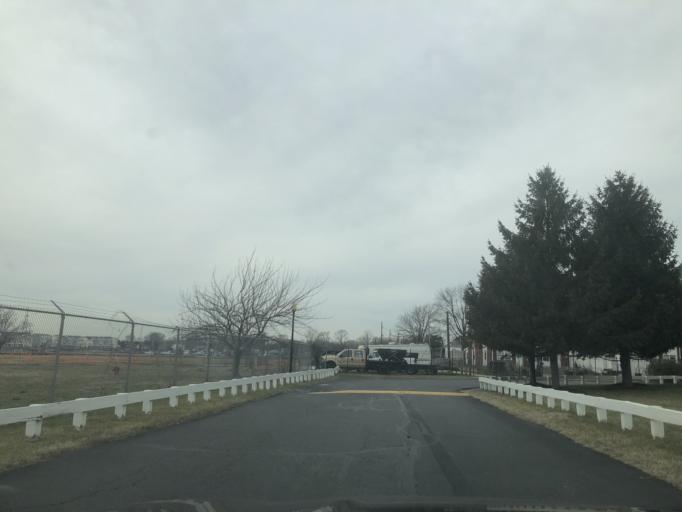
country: US
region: Maryland
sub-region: Baltimore County
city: Dundalk
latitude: 39.2548
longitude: -76.4880
